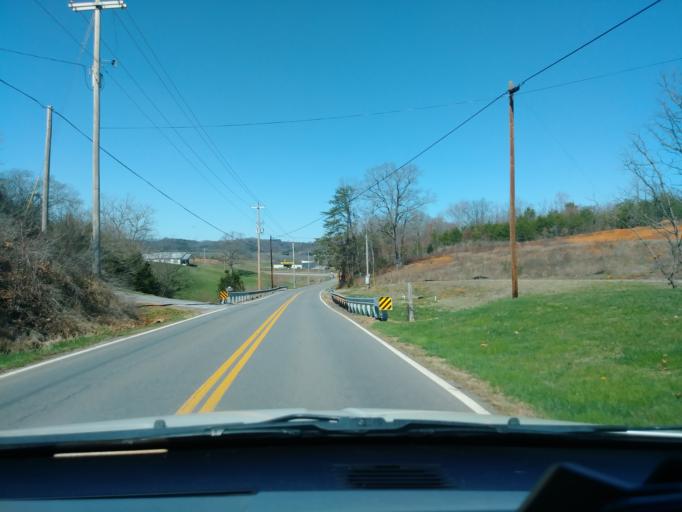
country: US
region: Tennessee
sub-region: Cocke County
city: Newport
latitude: 36.0017
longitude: -83.0889
